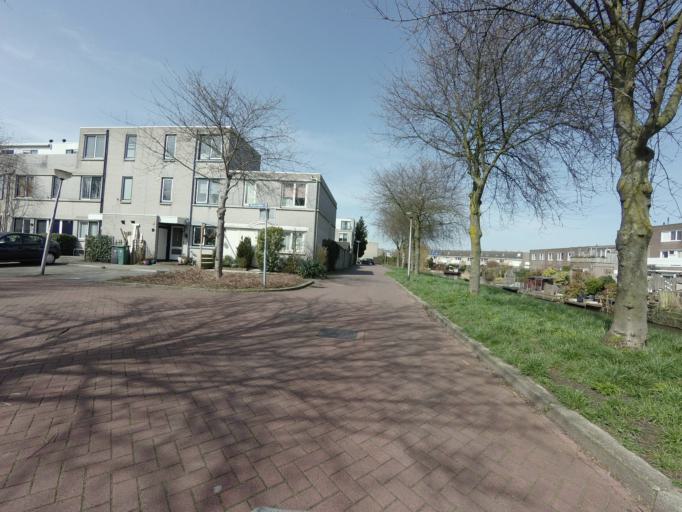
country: NL
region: South Holland
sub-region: Gemeente Zoetermeer
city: Zoetermeer
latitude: 52.0749
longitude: 4.5138
